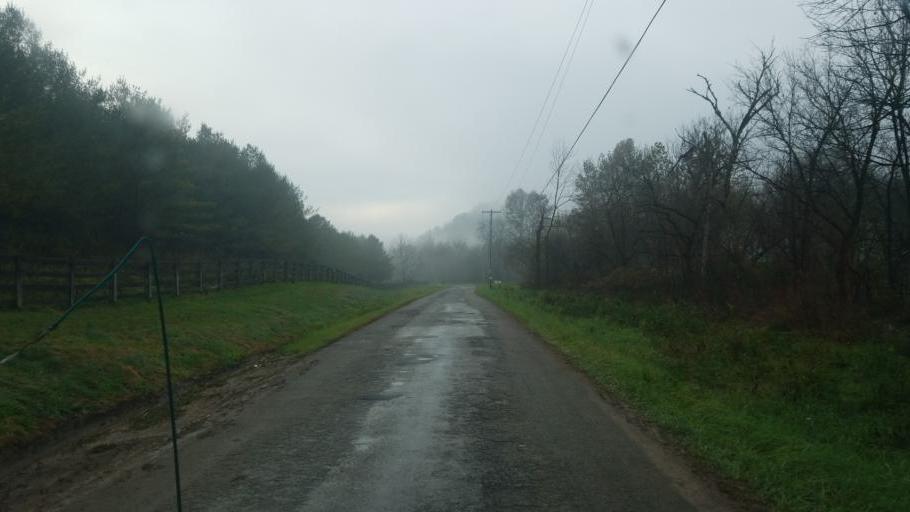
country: US
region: Ohio
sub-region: Athens County
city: Glouster
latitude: 39.4429
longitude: -81.9221
